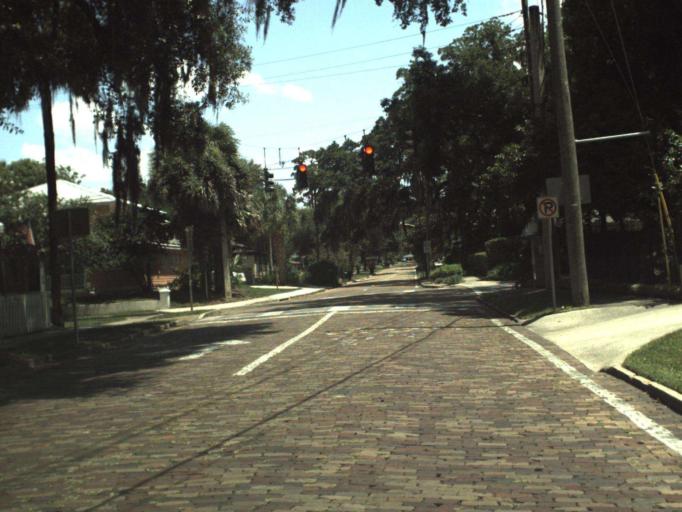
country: US
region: Florida
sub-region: Orange County
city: Orlando
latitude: 28.5418
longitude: -81.3631
